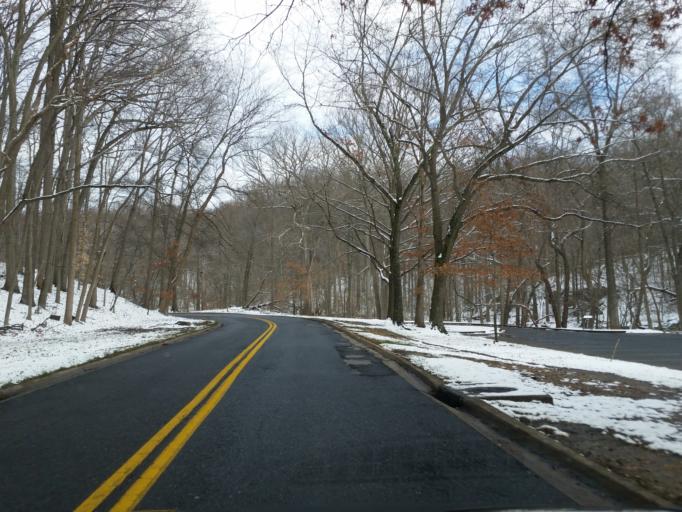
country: US
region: Maryland
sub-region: Montgomery County
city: Silver Spring
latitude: 38.9717
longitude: -77.0416
